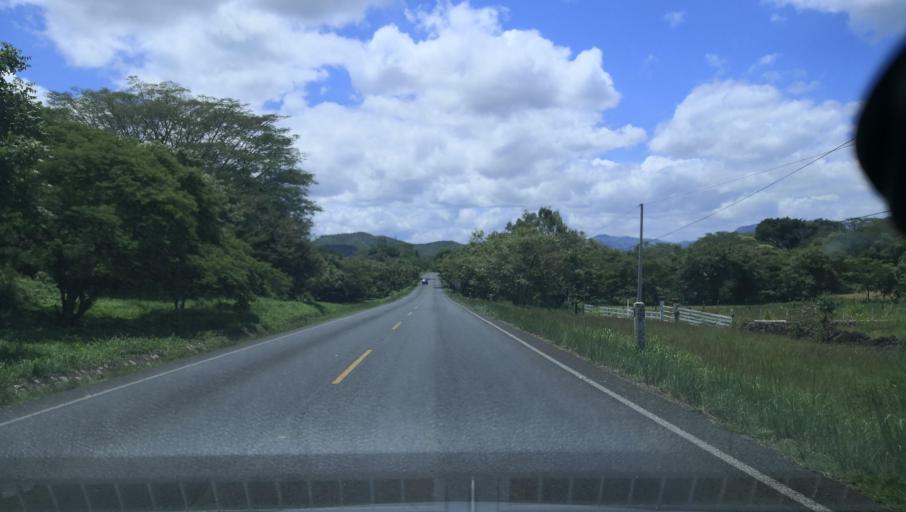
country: NI
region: Esteli
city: Condega
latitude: 13.2313
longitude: -86.3779
